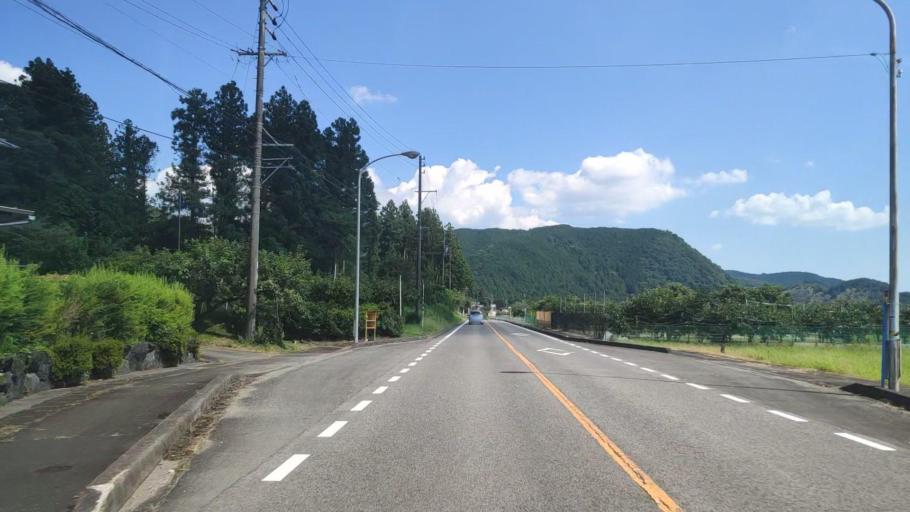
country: JP
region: Gifu
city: Godo
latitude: 35.5387
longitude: 136.6476
